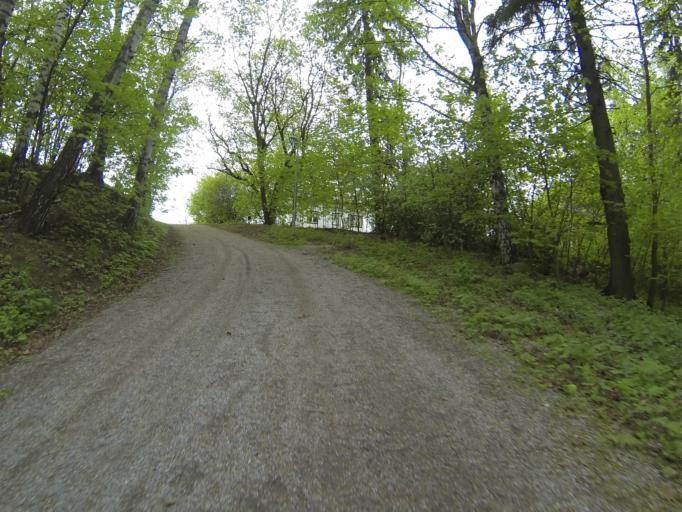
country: FI
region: Varsinais-Suomi
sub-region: Salo
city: Salo
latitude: 60.3750
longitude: 23.1247
